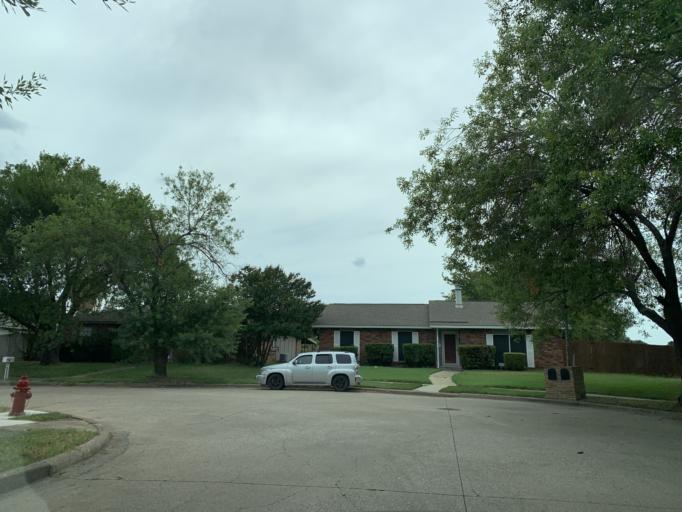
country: US
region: Texas
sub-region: Dallas County
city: Cedar Hill
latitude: 32.6490
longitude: -97.0293
